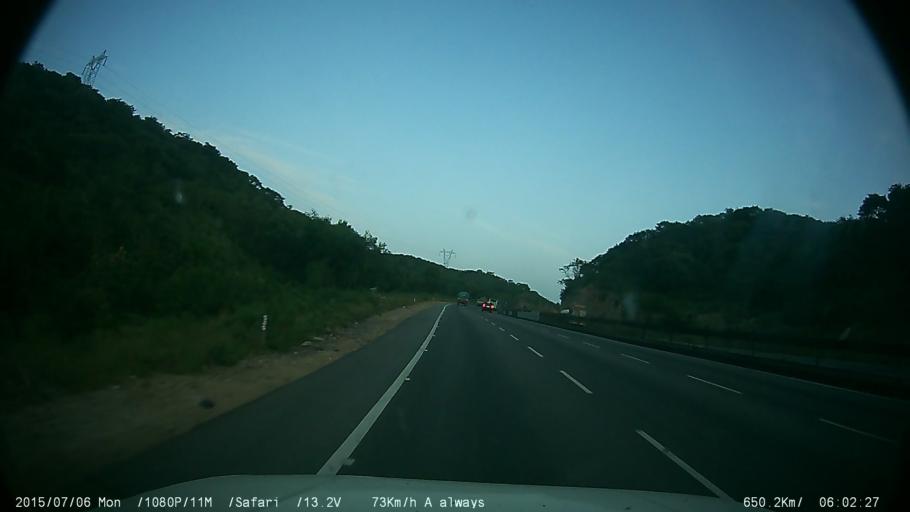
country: IN
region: Tamil Nadu
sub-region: Krishnagiri
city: Krishnagiri
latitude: 12.6058
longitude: 78.1072
